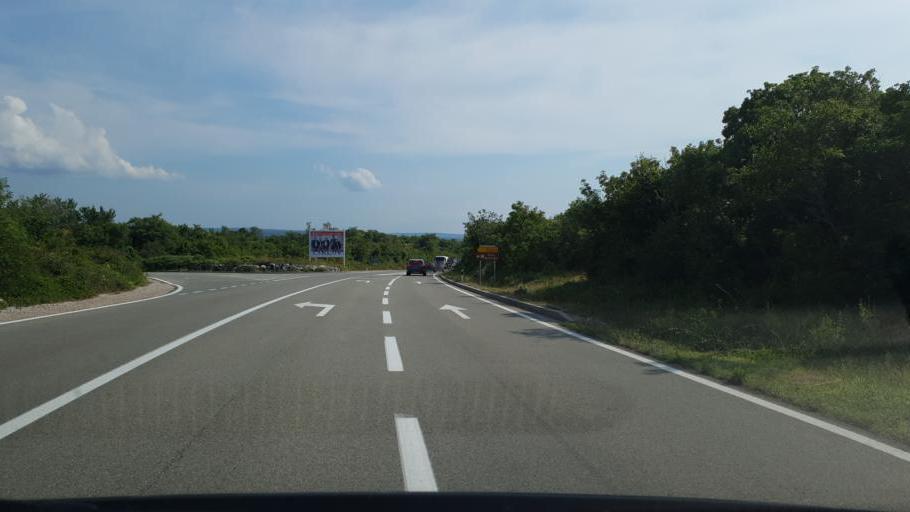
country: HR
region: Primorsko-Goranska
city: Omisalj
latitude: 45.2061
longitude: 14.5668
